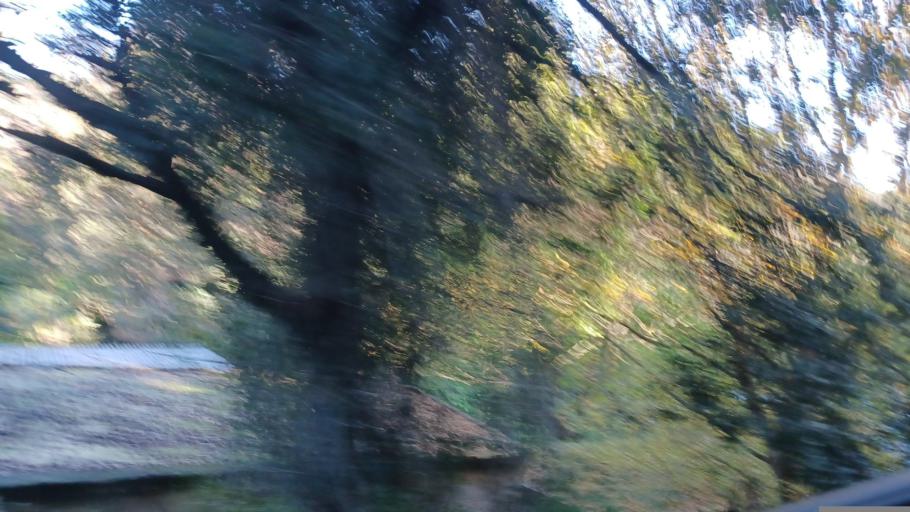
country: CY
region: Pafos
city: Mesogi
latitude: 34.8704
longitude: 32.5600
